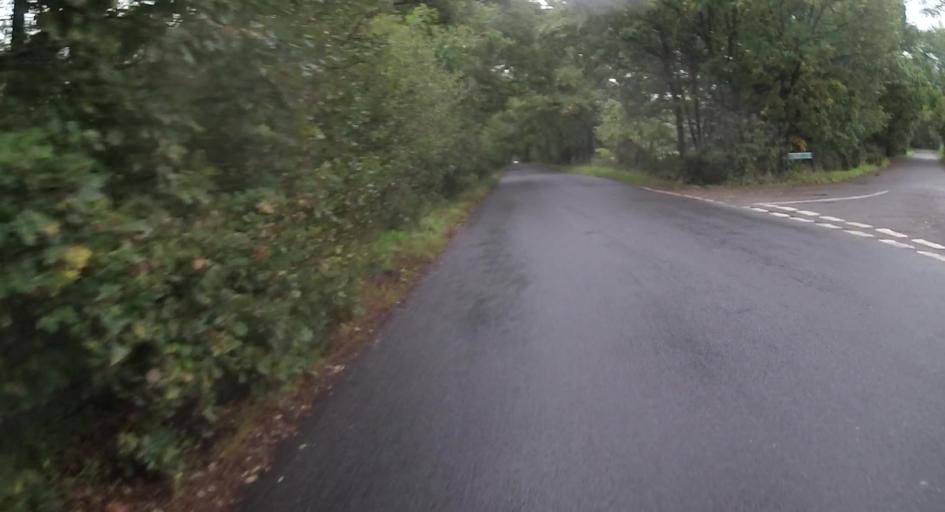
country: GB
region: England
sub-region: Hampshire
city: Tadley
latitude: 51.3600
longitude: -1.1802
